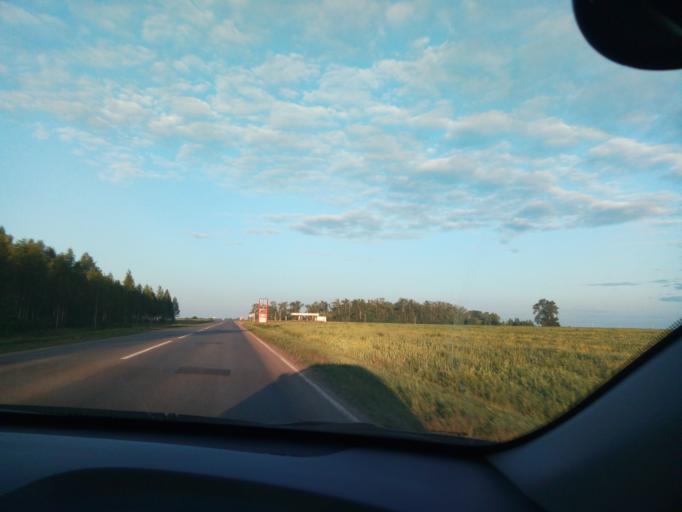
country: RU
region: Nizjnij Novgorod
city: Vyyezdnoye
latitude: 55.3407
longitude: 43.7484
